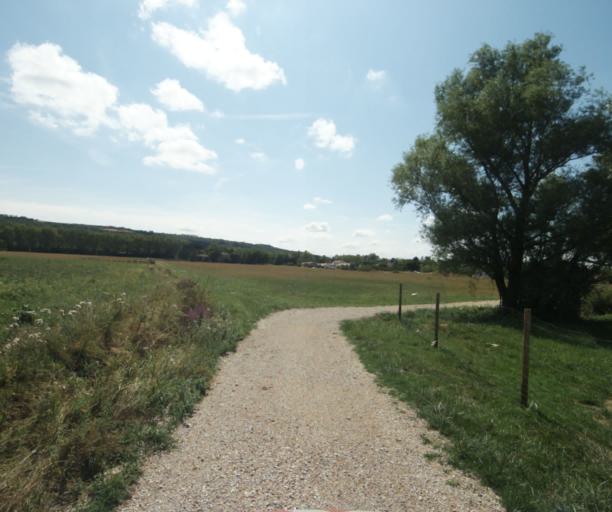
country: FR
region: Midi-Pyrenees
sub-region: Departement de la Haute-Garonne
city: Revel
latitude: 43.4574
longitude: 2.0209
